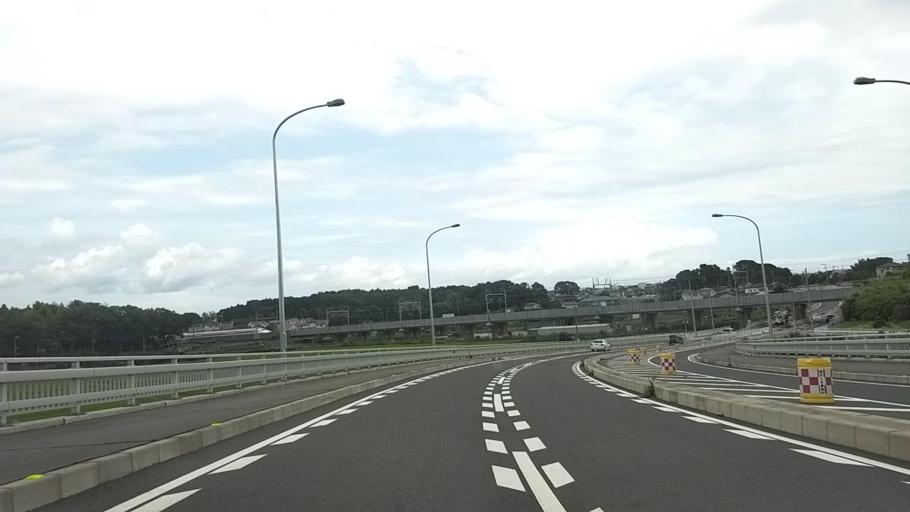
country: JP
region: Kanagawa
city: Atsugi
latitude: 35.4085
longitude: 139.4084
